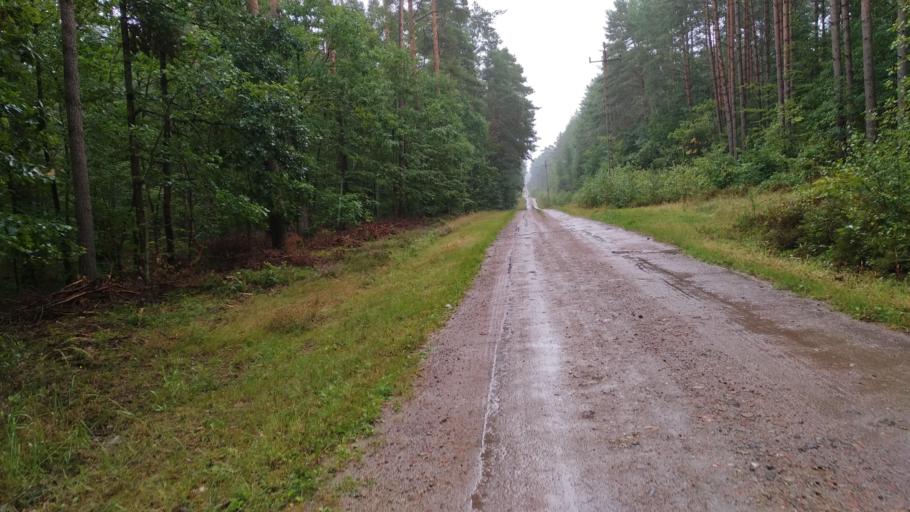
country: PL
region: Pomeranian Voivodeship
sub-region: Powiat wejherowski
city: Goscicino
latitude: 54.6242
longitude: 18.1461
